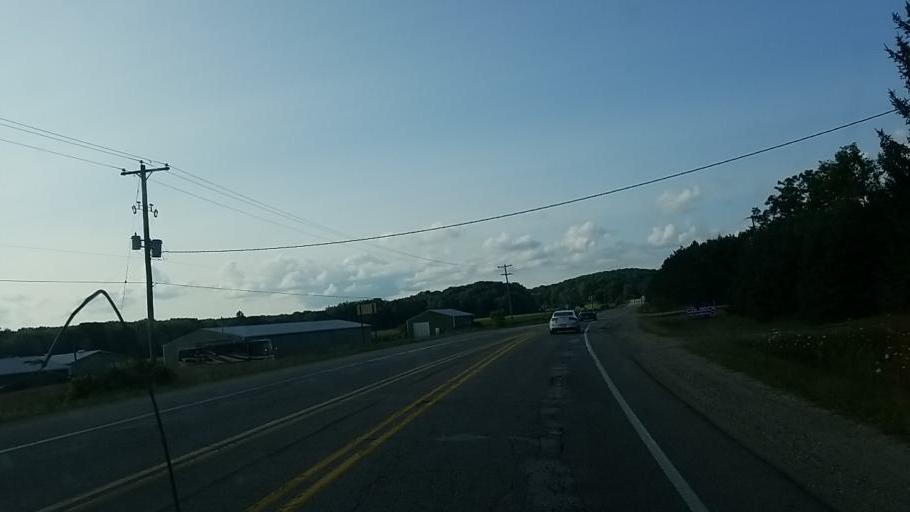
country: US
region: Michigan
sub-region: Kent County
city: Lowell
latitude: 42.9593
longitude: -85.3554
